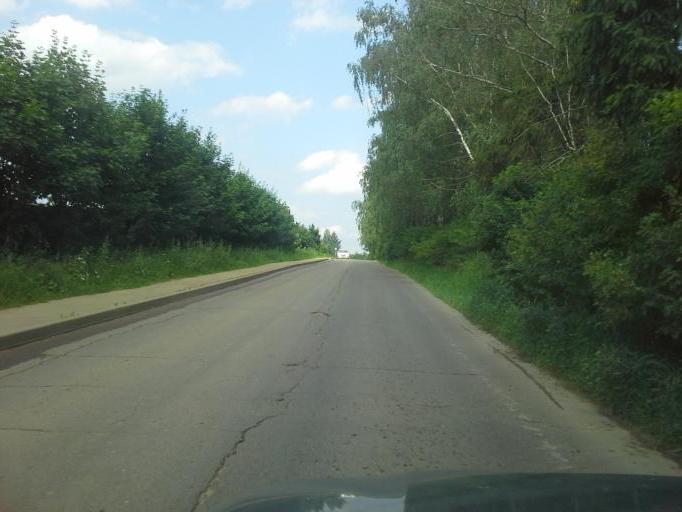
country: RU
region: Moskovskaya
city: Barvikha
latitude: 55.7216
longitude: 37.2820
